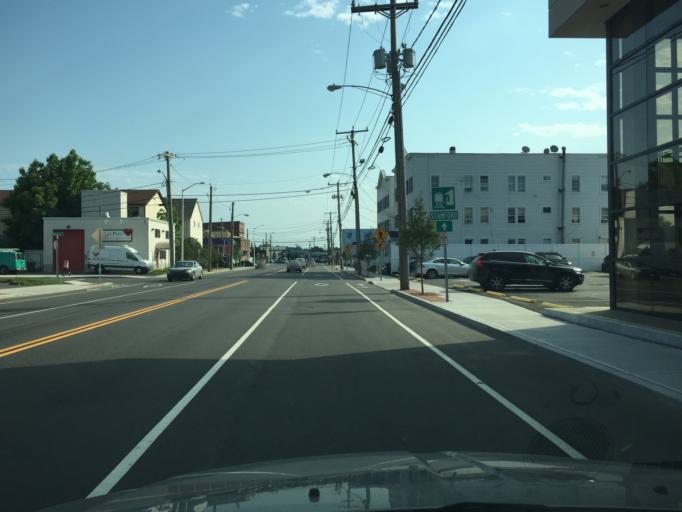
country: US
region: Connecticut
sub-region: Fairfield County
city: Stamford
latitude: 41.0528
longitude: -73.5259
